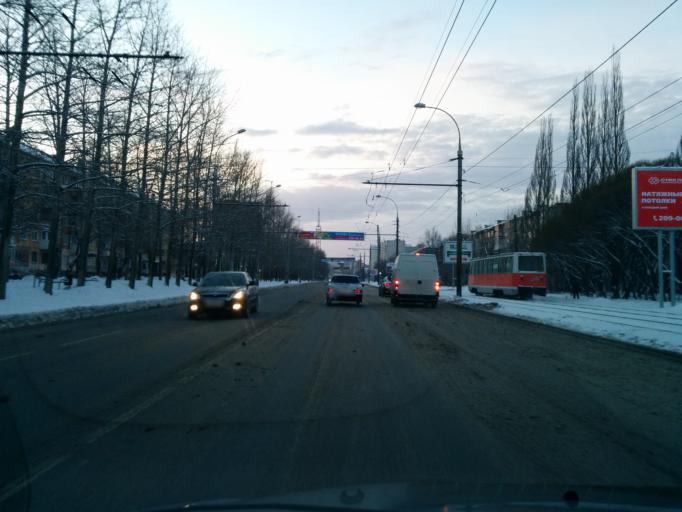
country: RU
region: Perm
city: Perm
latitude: 58.0029
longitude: 56.2866
